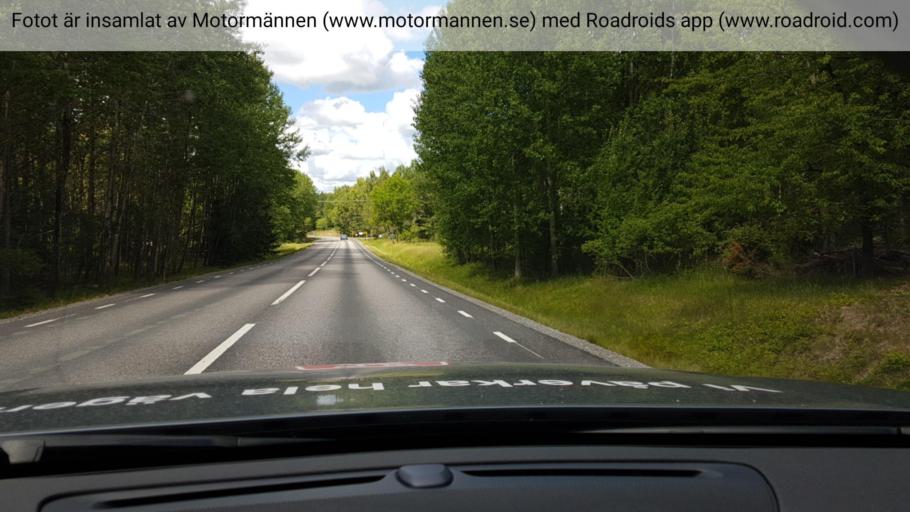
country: SE
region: Stockholm
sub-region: Varmdo Kommun
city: Mortnas
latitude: 59.3954
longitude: 18.4611
